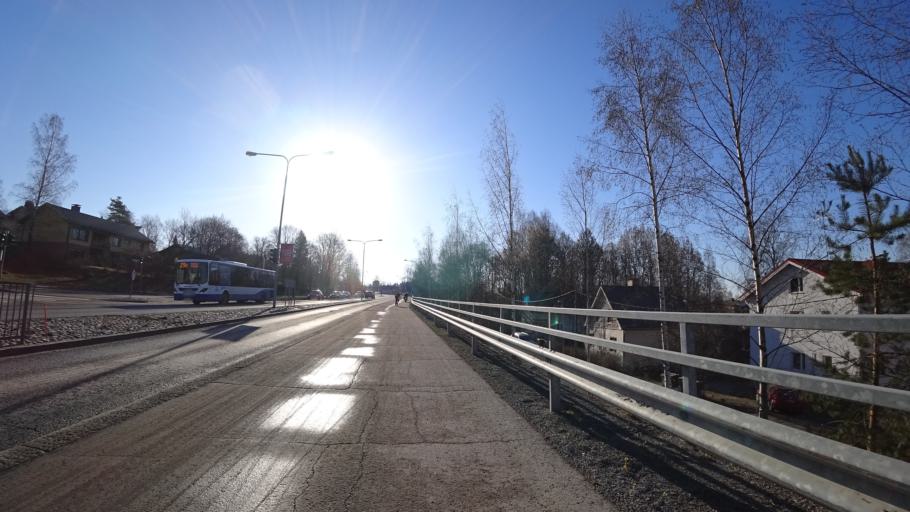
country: FI
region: Pirkanmaa
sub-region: Tampere
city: Pirkkala
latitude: 61.5068
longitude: 23.6950
